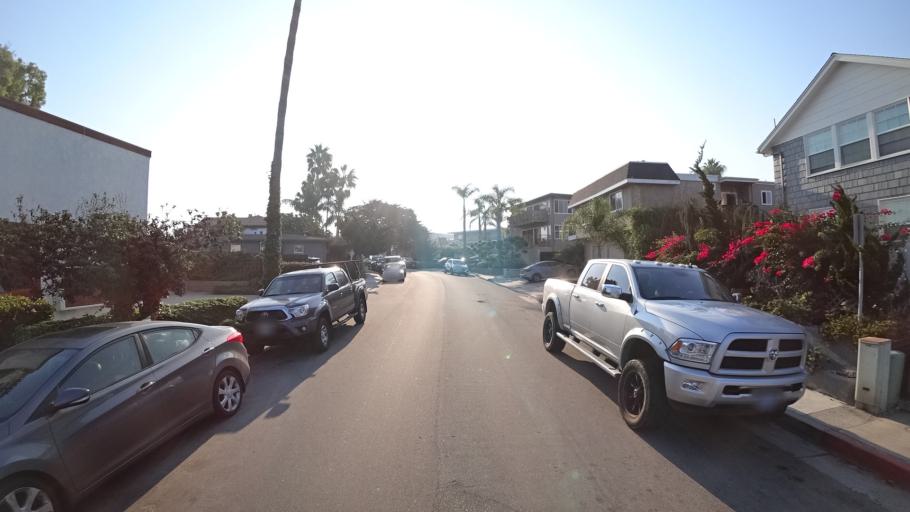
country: US
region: California
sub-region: Orange County
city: San Clemente
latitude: 33.4073
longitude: -117.6058
